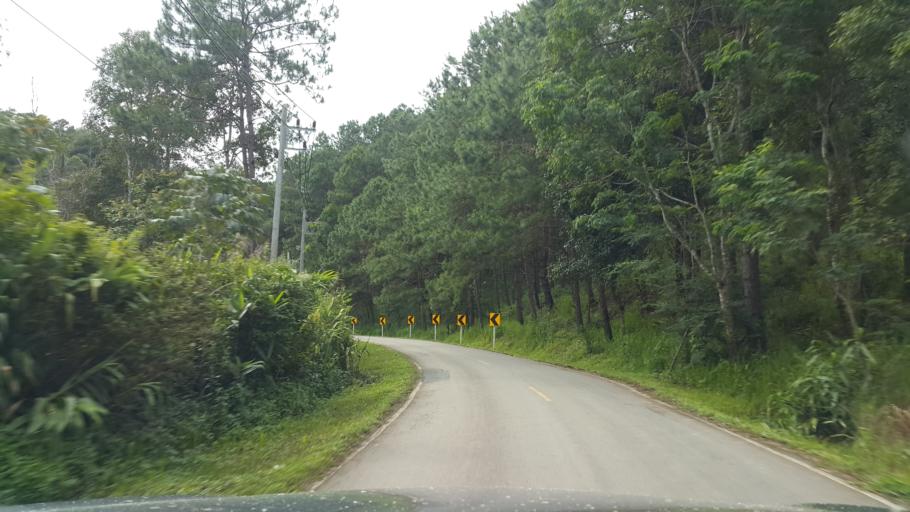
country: TH
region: Chiang Mai
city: Samoeng
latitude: 18.8861
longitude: 98.5030
